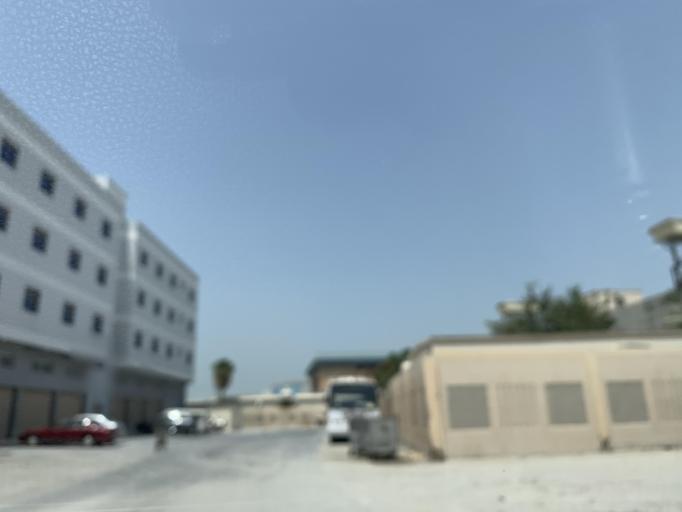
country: BH
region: Northern
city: Madinat `Isa
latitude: 26.1922
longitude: 50.5522
